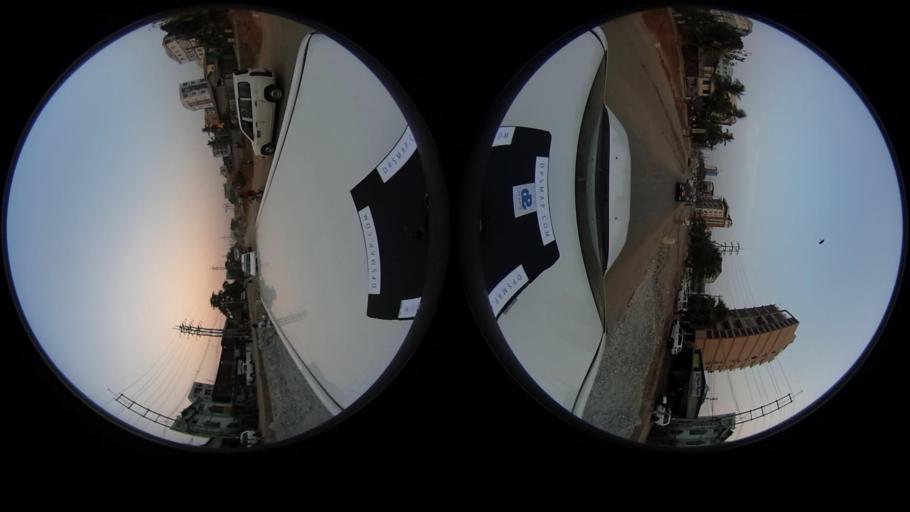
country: MM
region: Yangon
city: Yangon
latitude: 16.7829
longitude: 96.1817
